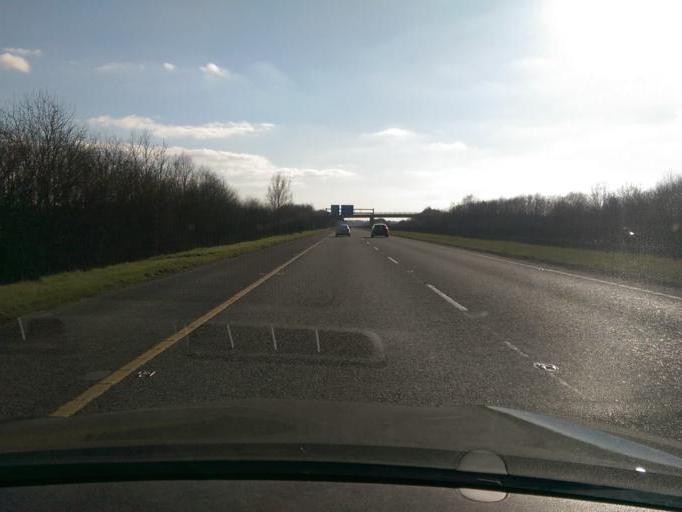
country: IE
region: Leinster
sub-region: Kildare
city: Kilcullen
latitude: 53.1880
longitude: -6.7303
